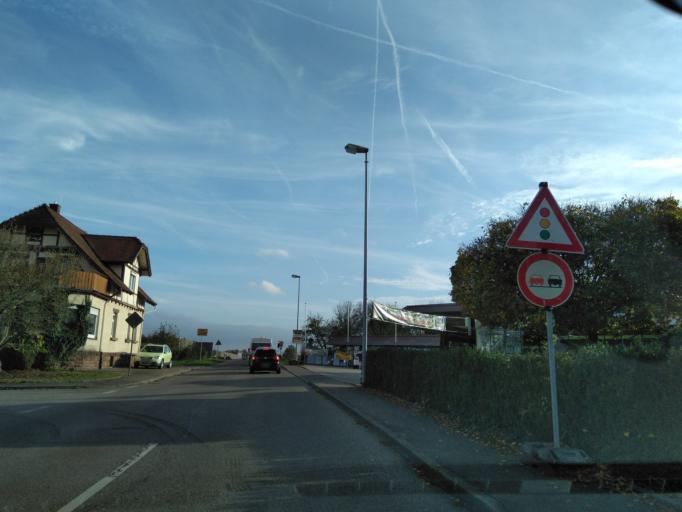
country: DE
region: Baden-Wuerttemberg
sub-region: Regierungsbezirk Stuttgart
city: Oberriexingen
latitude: 48.9573
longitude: 9.0678
